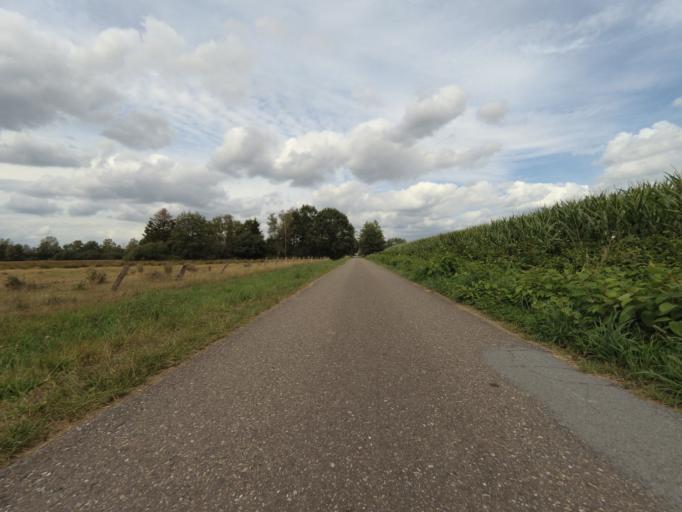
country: DE
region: North Rhine-Westphalia
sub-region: Regierungsbezirk Munster
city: Gronau
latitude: 52.1874
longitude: 6.9667
